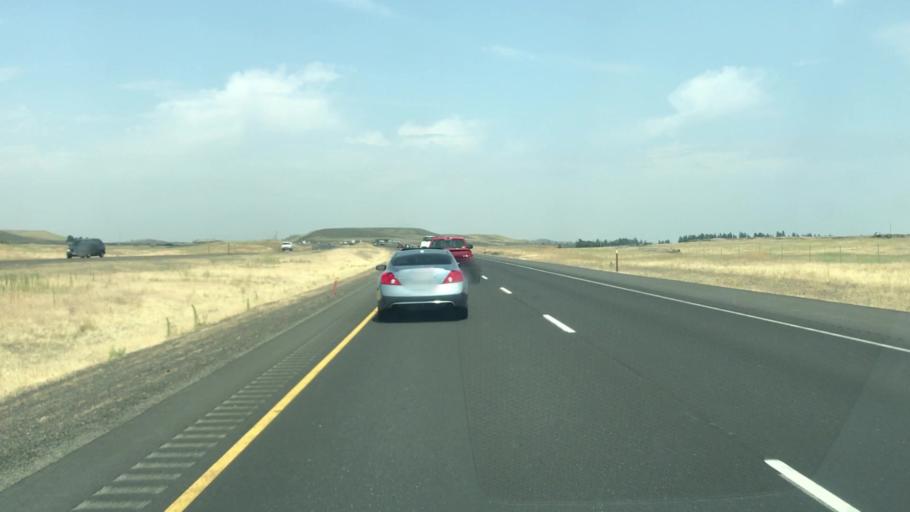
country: US
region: Washington
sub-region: Spokane County
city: Medical Lake
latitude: 47.3362
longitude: -117.9131
